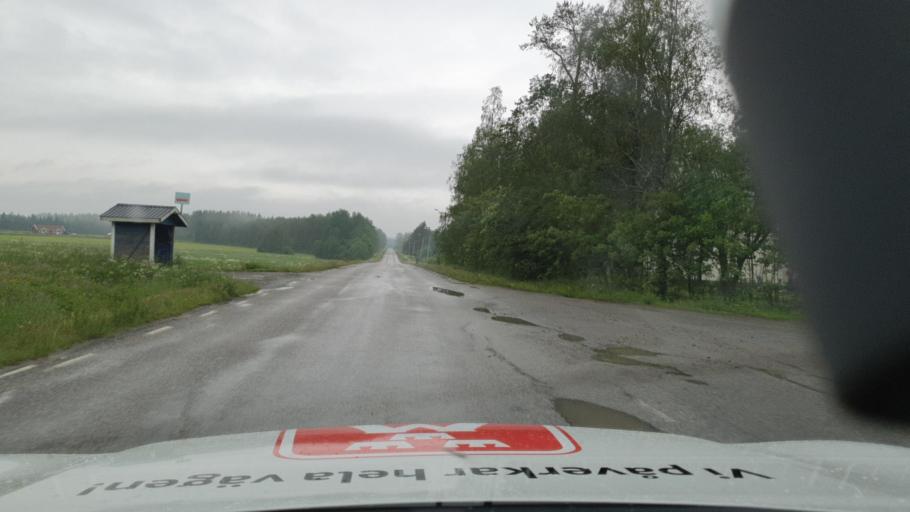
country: SE
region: Vaesterbotten
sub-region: Nordmalings Kommun
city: Nordmaling
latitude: 63.7913
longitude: 19.5489
